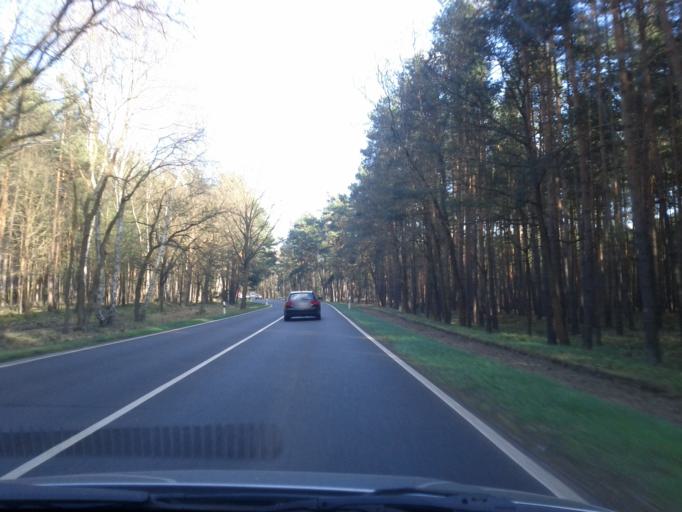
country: DE
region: Brandenburg
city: Rauen
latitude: 52.3849
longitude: 13.9645
